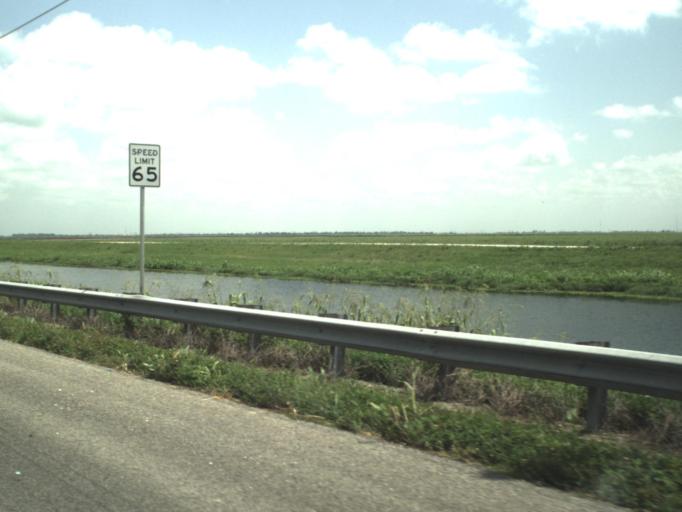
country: US
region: Florida
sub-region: Palm Beach County
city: South Bay
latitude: 26.6212
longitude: -80.7118
